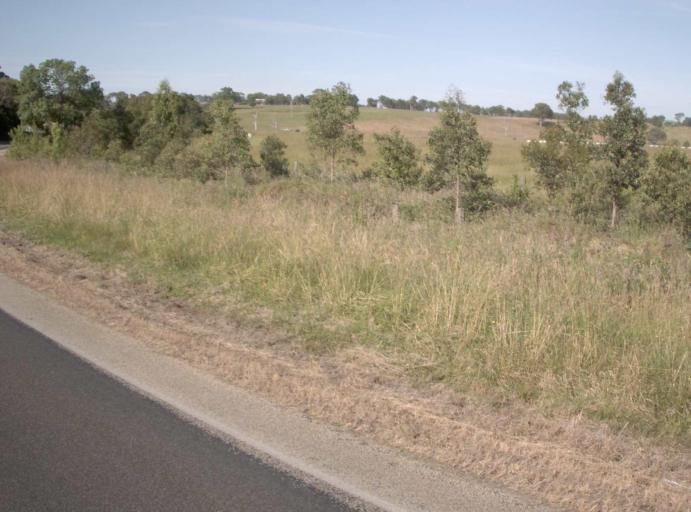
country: AU
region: Victoria
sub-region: East Gippsland
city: Lakes Entrance
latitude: -37.8474
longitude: 147.8506
